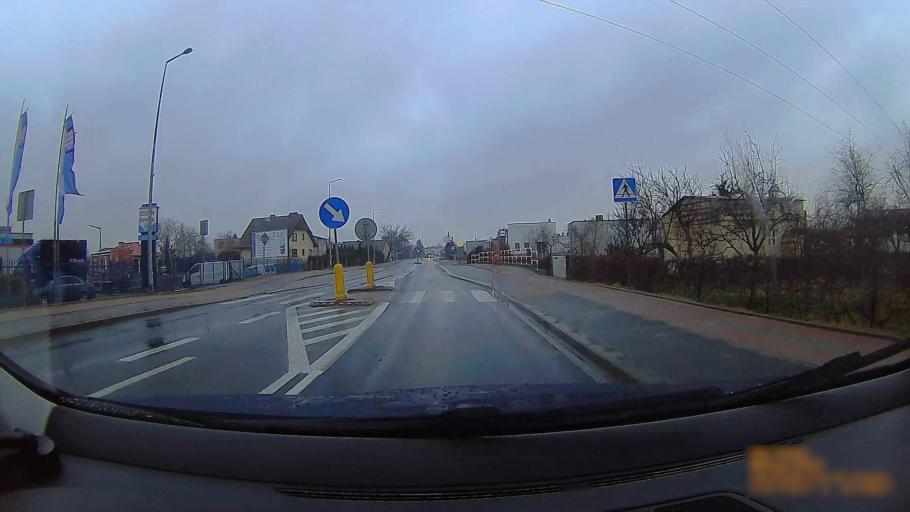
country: PL
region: Greater Poland Voivodeship
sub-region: Konin
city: Konin
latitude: 52.1942
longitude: 18.2633
